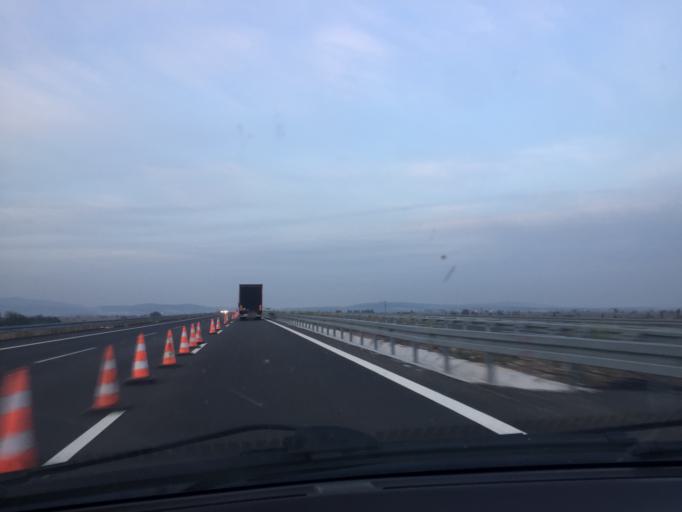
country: TR
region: Manisa
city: Halitpasa
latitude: 38.7305
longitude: 27.6553
